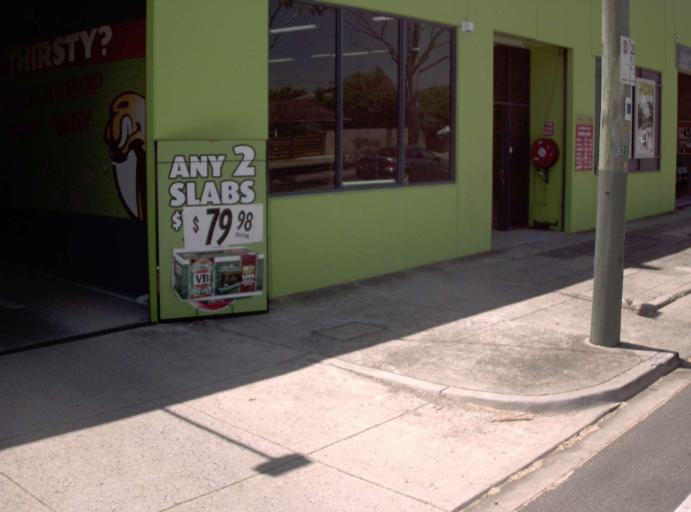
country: AU
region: Victoria
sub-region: Glen Eira
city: Caulfield South
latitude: -37.9021
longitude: 145.0264
